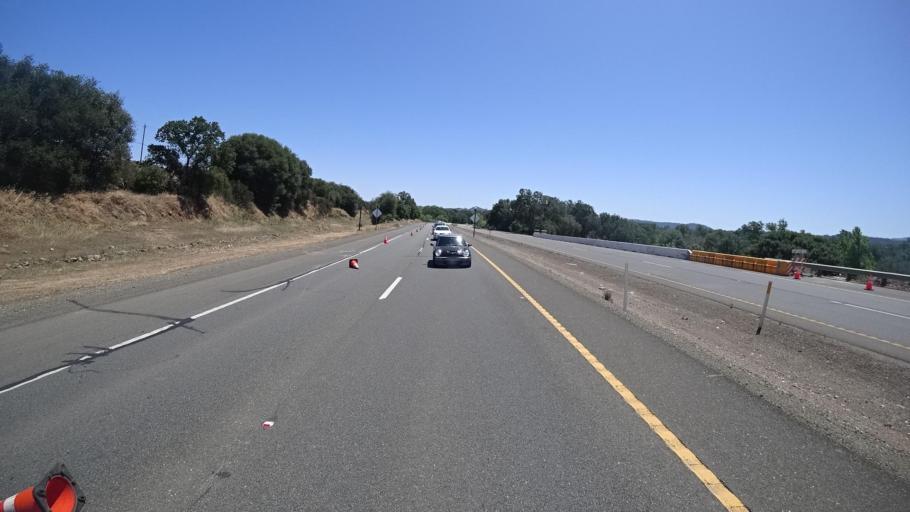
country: US
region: California
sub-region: Lake County
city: Lower Lake
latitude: 38.9276
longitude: -122.6173
